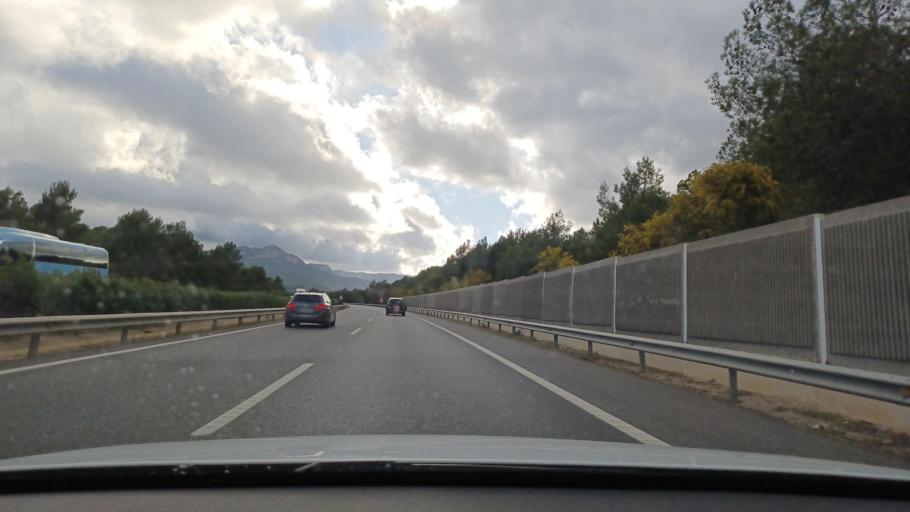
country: ES
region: Catalonia
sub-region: Provincia de Tarragona
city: Colldejou
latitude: 41.0359
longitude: 0.9238
